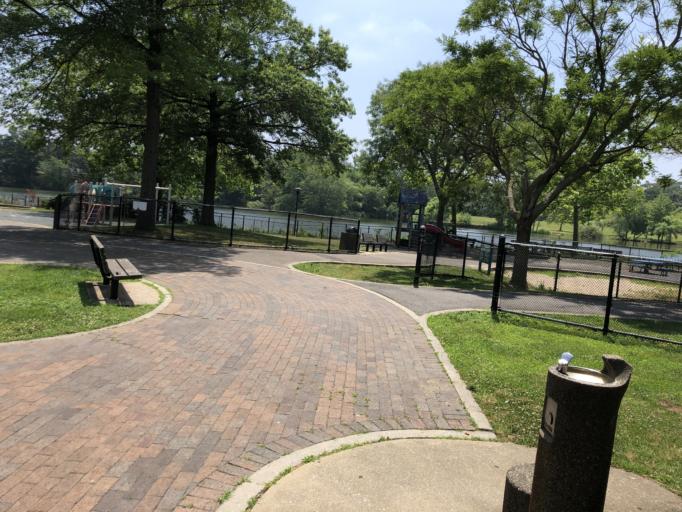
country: US
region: New York
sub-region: Nassau County
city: Hewlett
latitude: 40.6444
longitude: -73.6883
